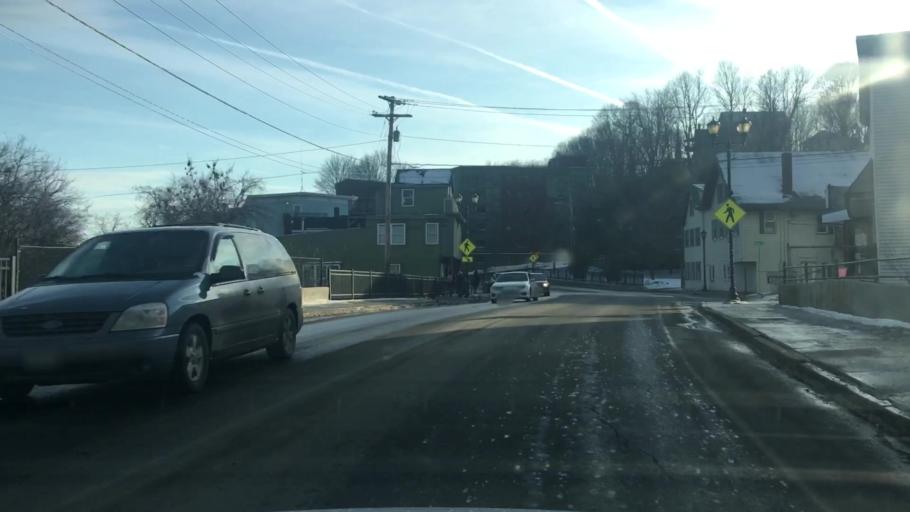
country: US
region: Maine
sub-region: Kennebec County
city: Augusta
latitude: 44.3206
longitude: -69.7733
